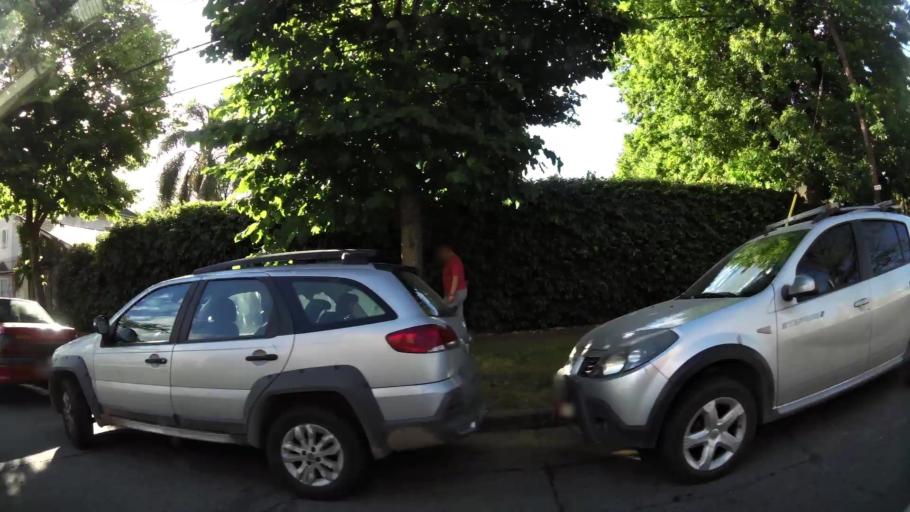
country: AR
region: Buenos Aires
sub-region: Partido de General San Martin
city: General San Martin
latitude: -34.5473
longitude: -58.5589
